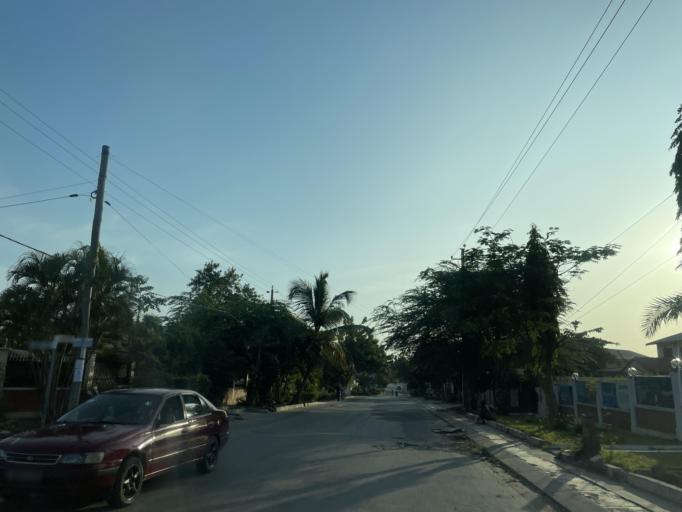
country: AO
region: Luanda
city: Luanda
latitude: -8.9091
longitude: 13.2287
